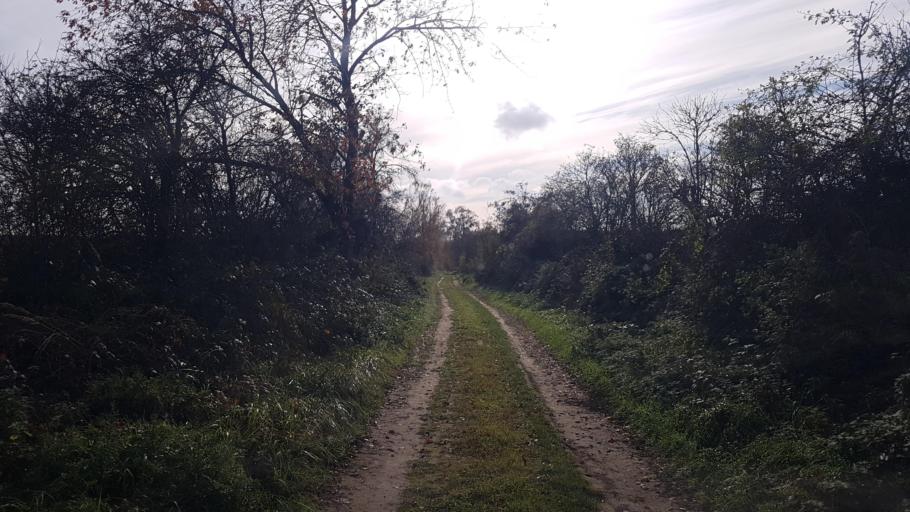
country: DE
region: Saxony-Anhalt
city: Zahna
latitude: 51.9730
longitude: 12.8380
